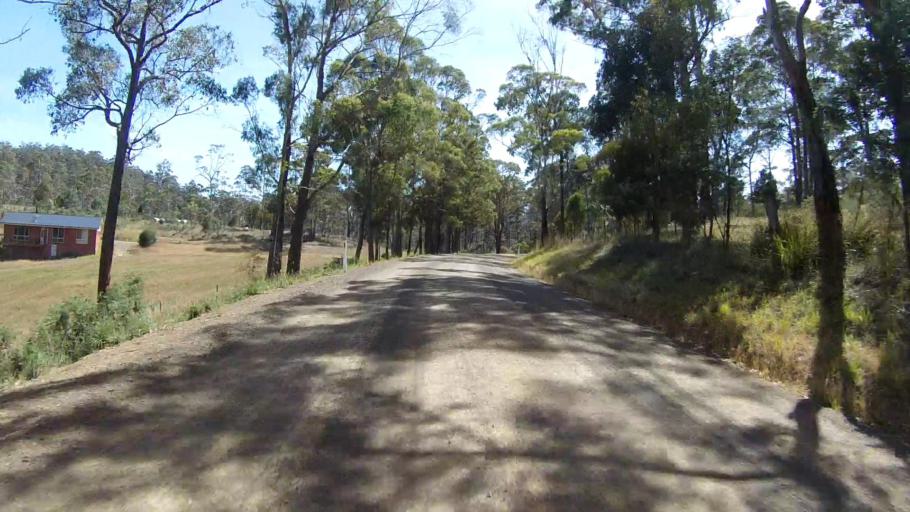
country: AU
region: Tasmania
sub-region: Sorell
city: Sorell
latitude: -42.7514
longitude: 147.7119
